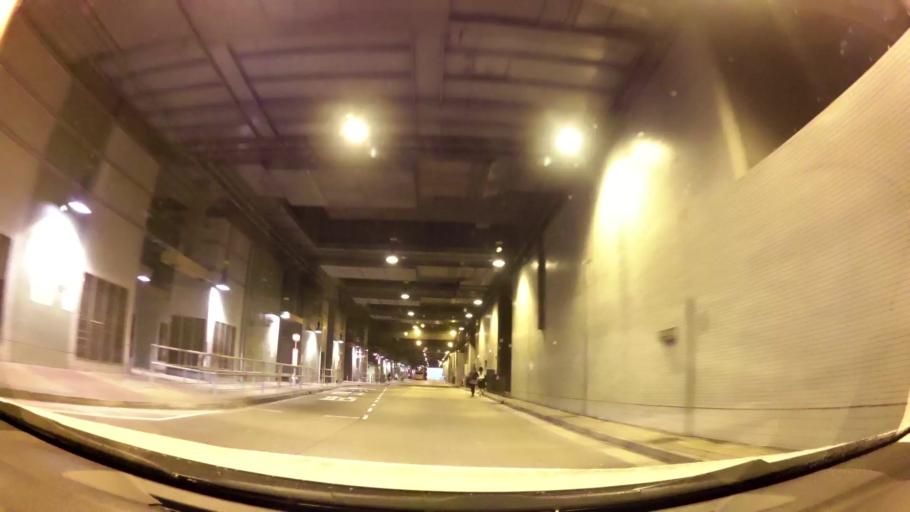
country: HK
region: Tsuen Wan
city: Tsuen Wan
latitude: 22.3676
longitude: 114.1109
